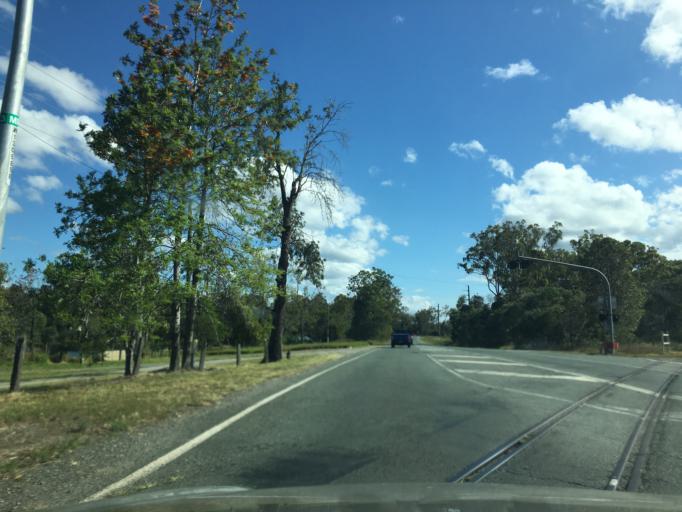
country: AU
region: Queensland
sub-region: Logan
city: Chambers Flat
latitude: -27.7785
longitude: 153.1014
